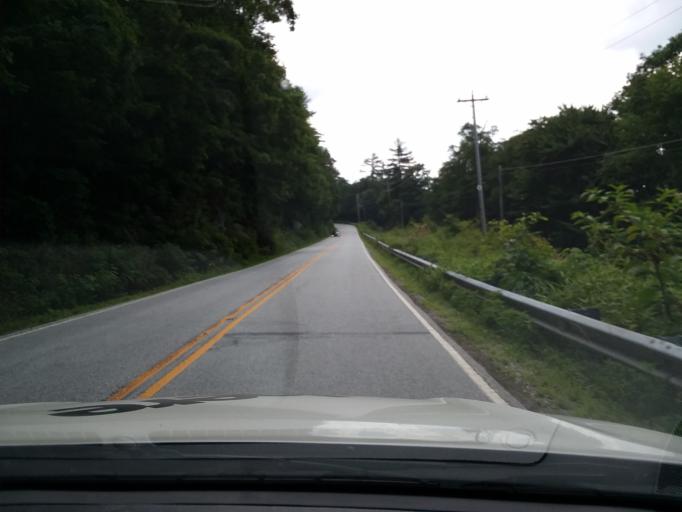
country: US
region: Georgia
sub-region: Rabun County
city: Mountain City
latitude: 35.0288
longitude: -83.2810
